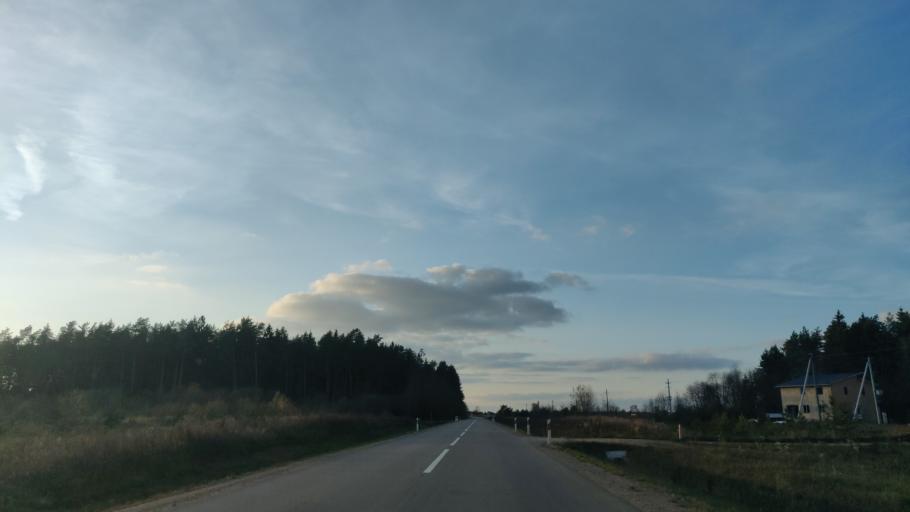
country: LT
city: Lentvaris
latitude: 54.5978
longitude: 25.0283
